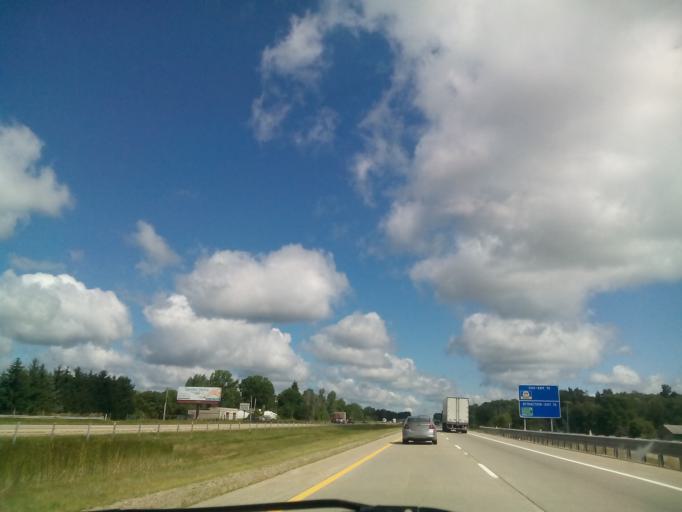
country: US
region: Michigan
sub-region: Genesee County
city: Linden
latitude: 42.7229
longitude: -83.7629
